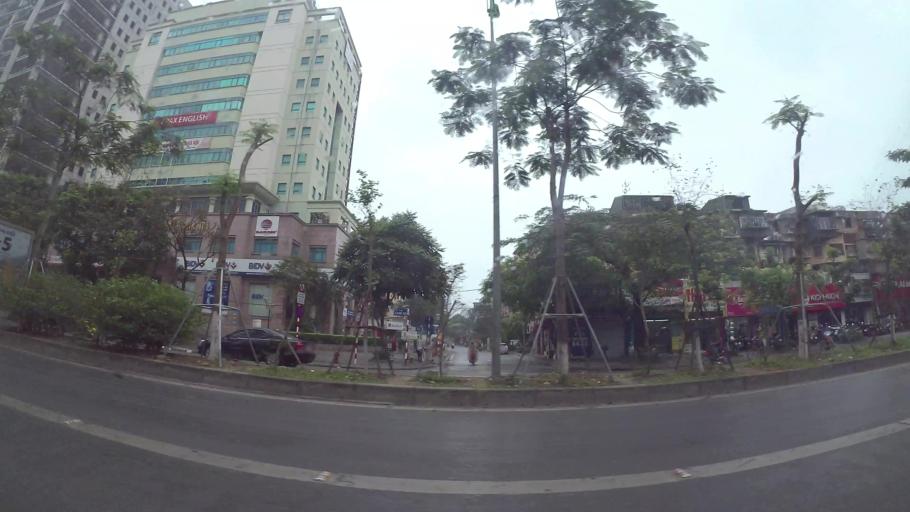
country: VN
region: Ha Noi
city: Dong Da
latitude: 21.0195
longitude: 105.8171
